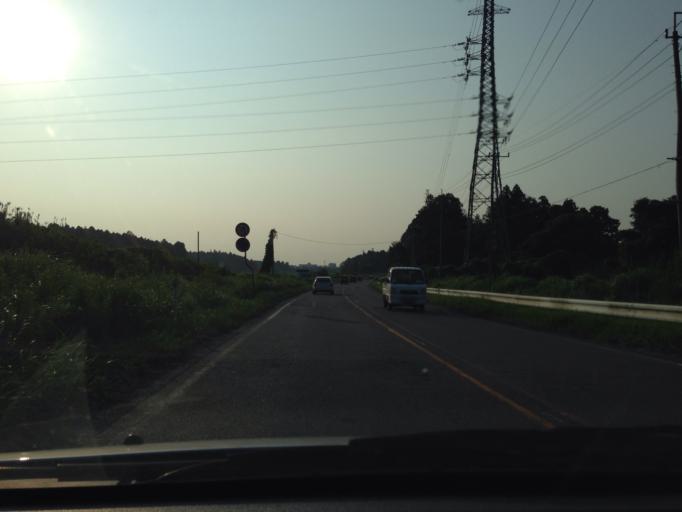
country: JP
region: Ibaraki
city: Ami
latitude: 36.0232
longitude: 140.2390
